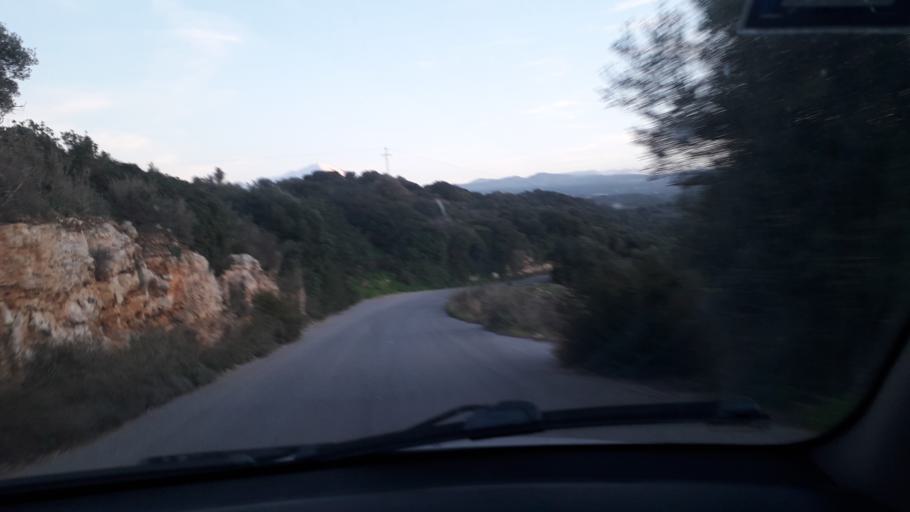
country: GR
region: Crete
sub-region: Nomos Rethymnis
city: Panormos
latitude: 35.3839
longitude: 24.6233
